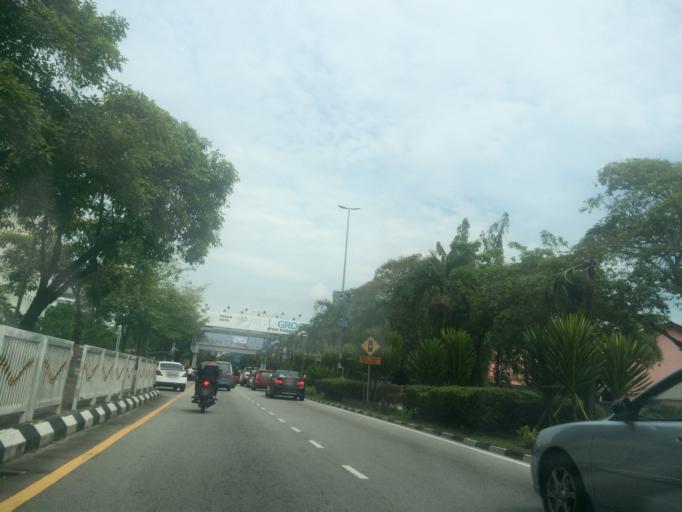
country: MY
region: Perak
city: Ipoh
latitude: 4.6044
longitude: 101.0915
